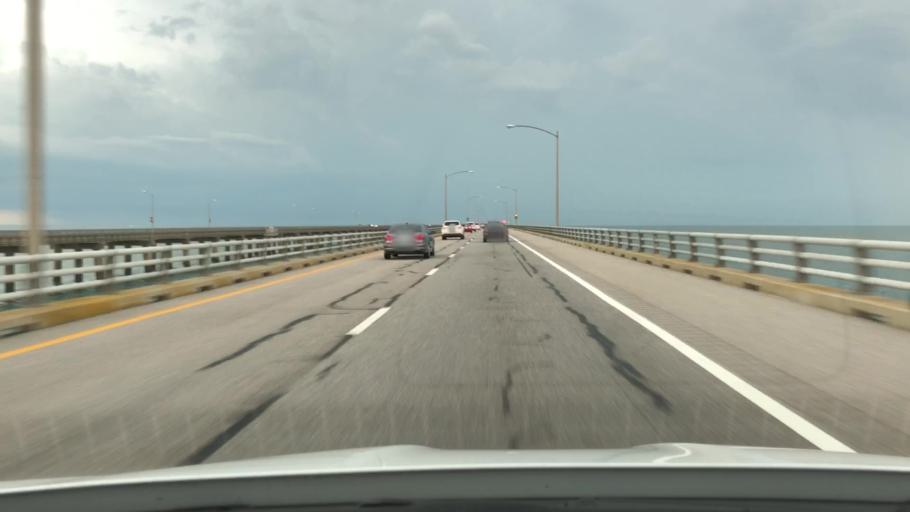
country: US
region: Virginia
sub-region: Northampton County
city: Cape Charles
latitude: 37.0736
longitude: -76.0254
